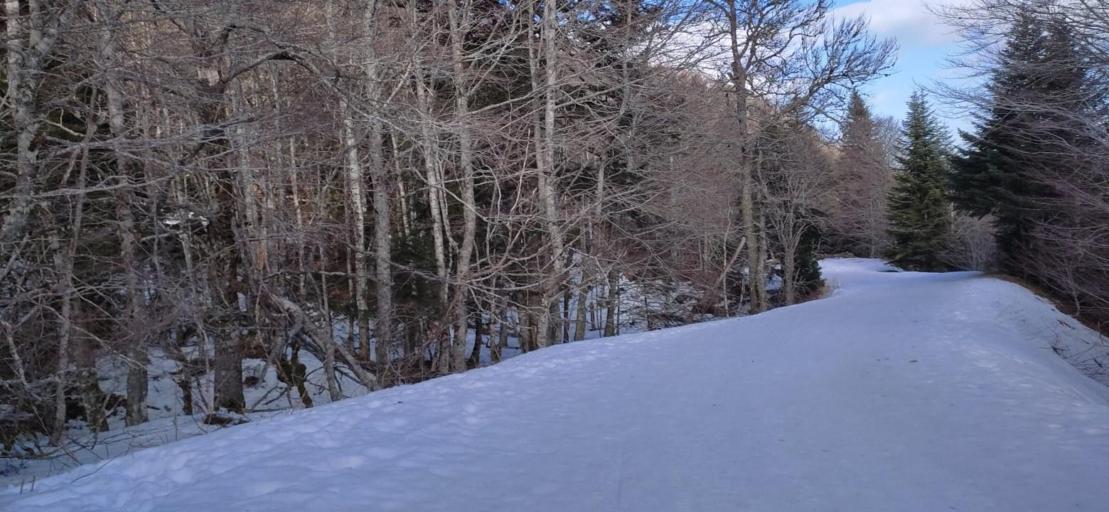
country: FR
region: Auvergne
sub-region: Departement du Puy-de-Dome
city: Mont-Dore
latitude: 45.5516
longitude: 2.8091
